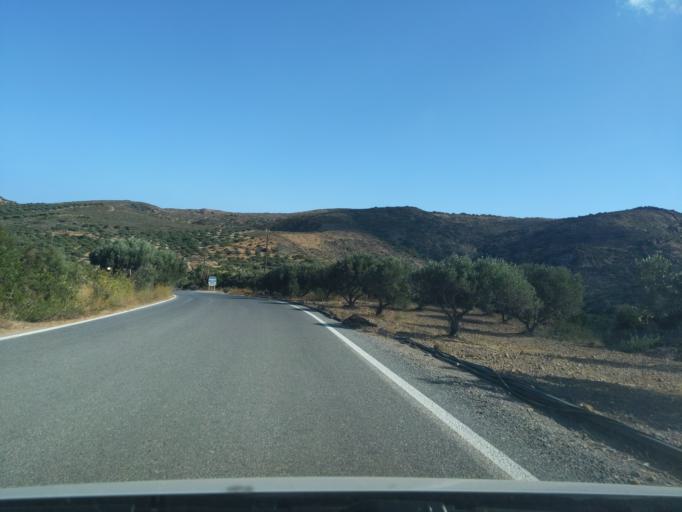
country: GR
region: Crete
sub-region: Nomos Lasithiou
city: Palekastro
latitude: 35.2205
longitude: 26.2587
